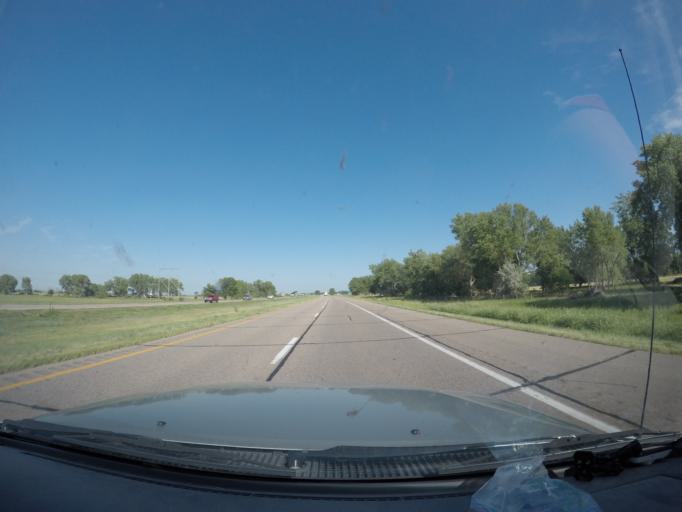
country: US
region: Nebraska
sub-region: Buffalo County
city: Kearney
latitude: 40.6784
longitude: -99.2779
